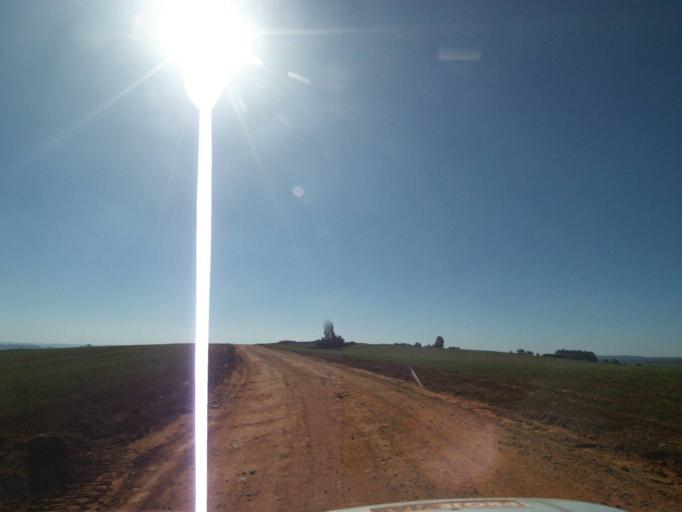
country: BR
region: Parana
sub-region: Tibagi
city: Tibagi
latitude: -24.5665
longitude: -50.6262
